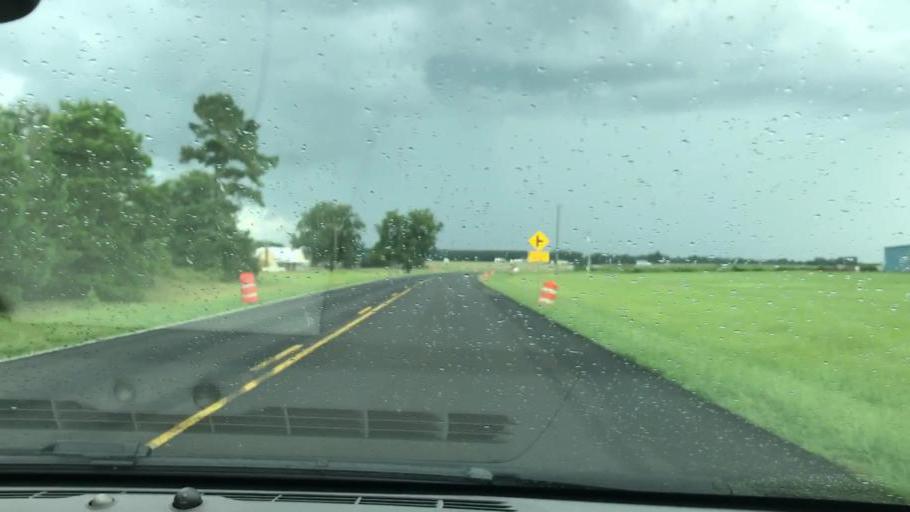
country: US
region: Georgia
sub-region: Clay County
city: Fort Gaines
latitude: 31.4932
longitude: -85.0183
